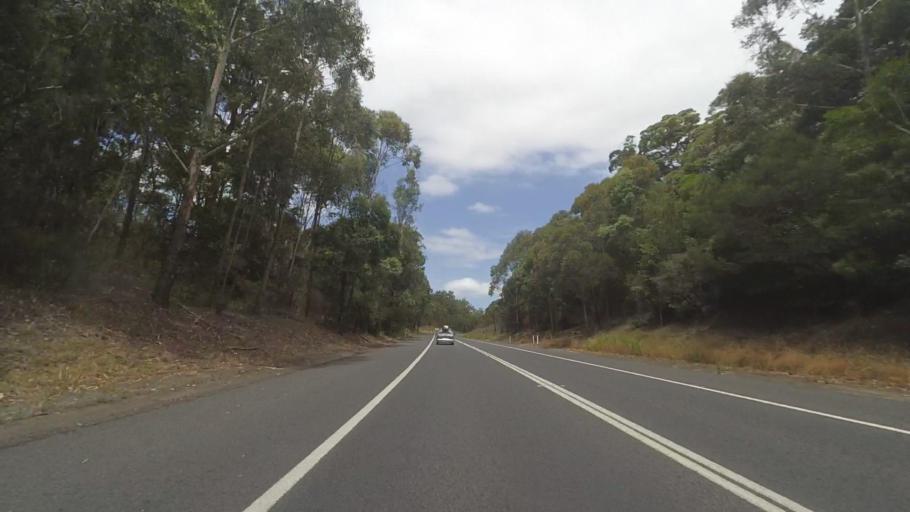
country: AU
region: New South Wales
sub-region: Shoalhaven Shire
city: Milton
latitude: -35.2355
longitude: 150.4310
